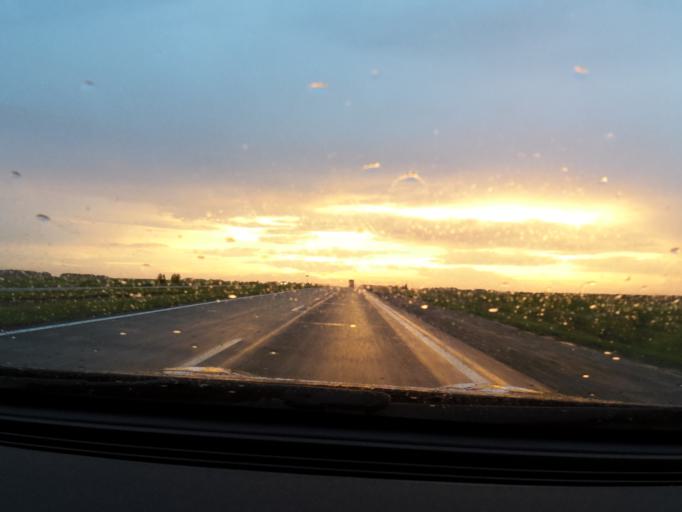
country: RU
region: Tatarstan
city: Yelabuga
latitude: 55.7874
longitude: 52.1665
